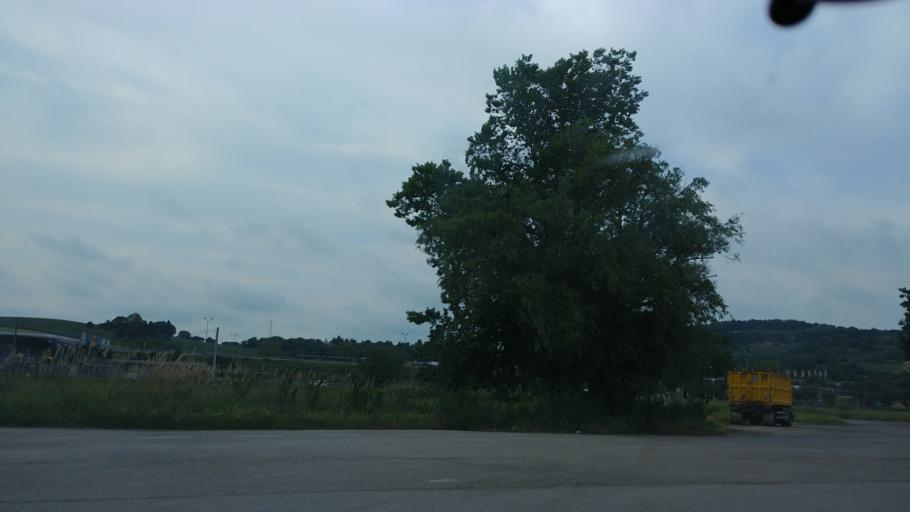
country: IT
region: The Marches
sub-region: Provincia di Pesaro e Urbino
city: Villa Ceccolini
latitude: 43.8959
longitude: 12.8427
